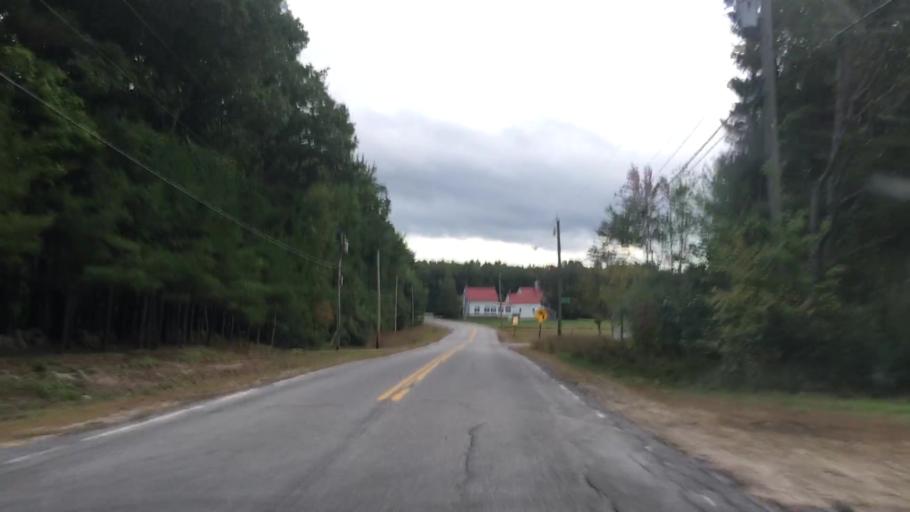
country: US
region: Maine
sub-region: York County
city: Parsonsfield
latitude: 43.7018
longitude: -70.9819
